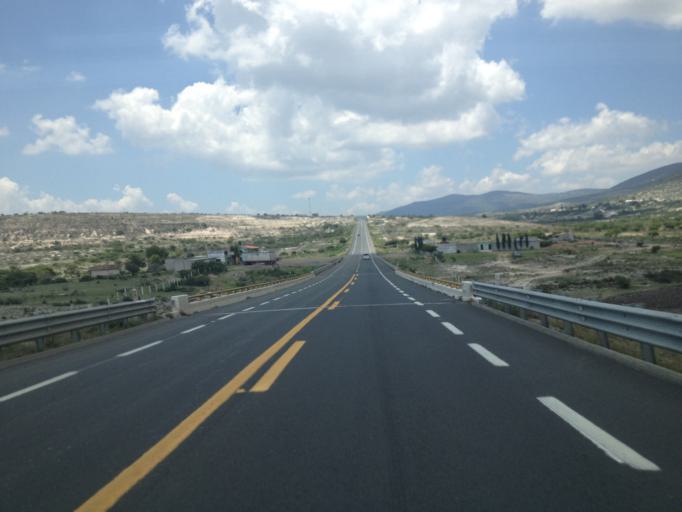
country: MX
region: Oaxaca
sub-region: Villa Tejupam de la Union
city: Villa Tejupam de la Union
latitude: 17.9263
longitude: -97.3584
